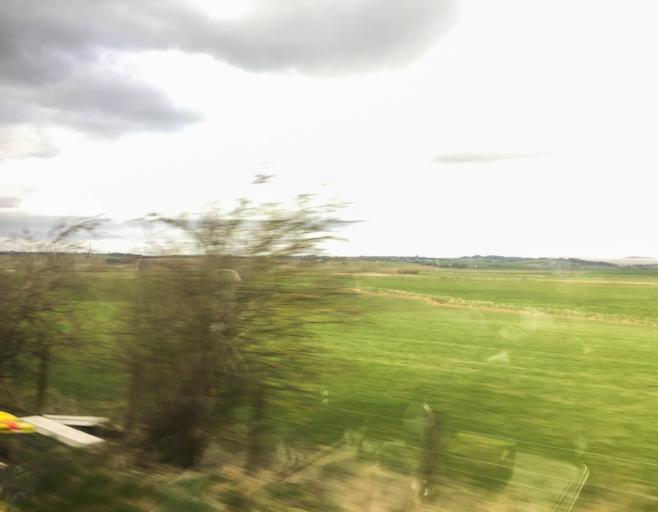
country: GB
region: Scotland
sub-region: South Lanarkshire
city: Carnwath
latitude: 55.6701
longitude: -3.6395
